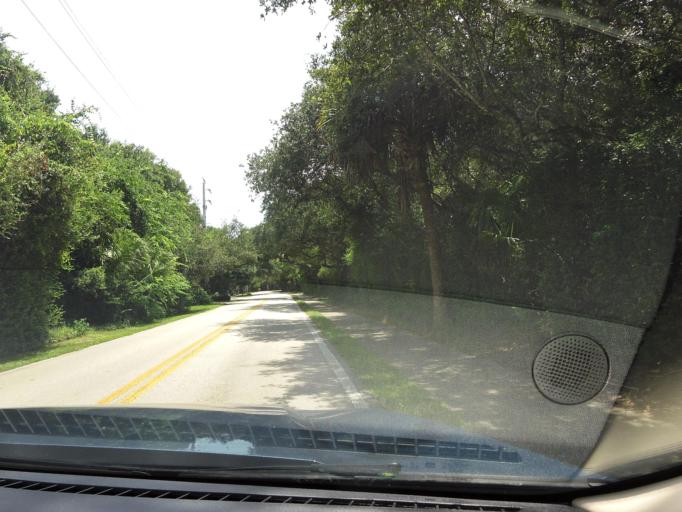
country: US
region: Florida
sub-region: Volusia County
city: Ponce Inlet
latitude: 29.0922
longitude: -80.9368
